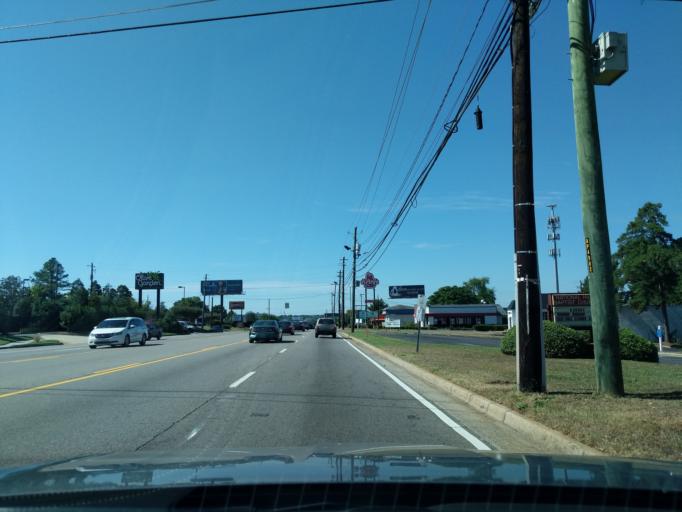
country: US
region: Georgia
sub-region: Columbia County
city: Martinez
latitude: 33.5092
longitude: -82.0248
